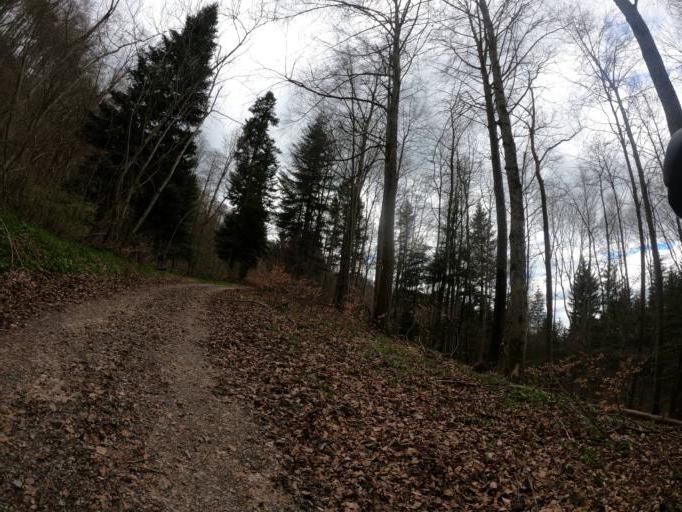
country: DE
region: Baden-Wuerttemberg
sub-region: Tuebingen Region
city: Jungingen
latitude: 48.3578
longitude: 9.0595
